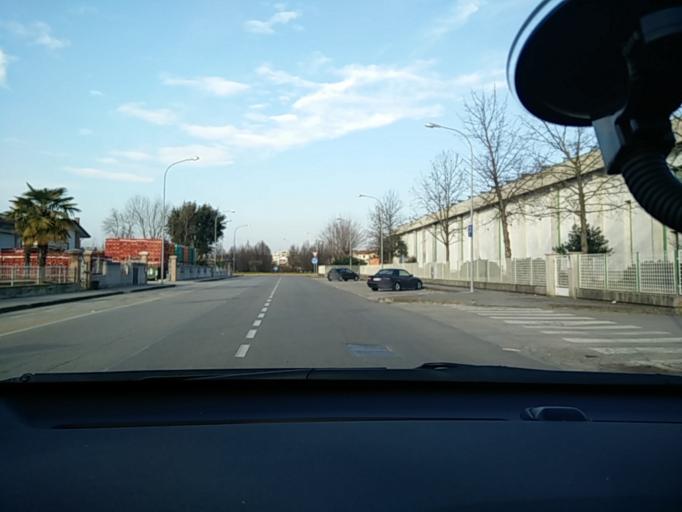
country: IT
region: Veneto
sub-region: Provincia di Venezia
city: San Dona di Piave
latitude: 45.6229
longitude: 12.5881
